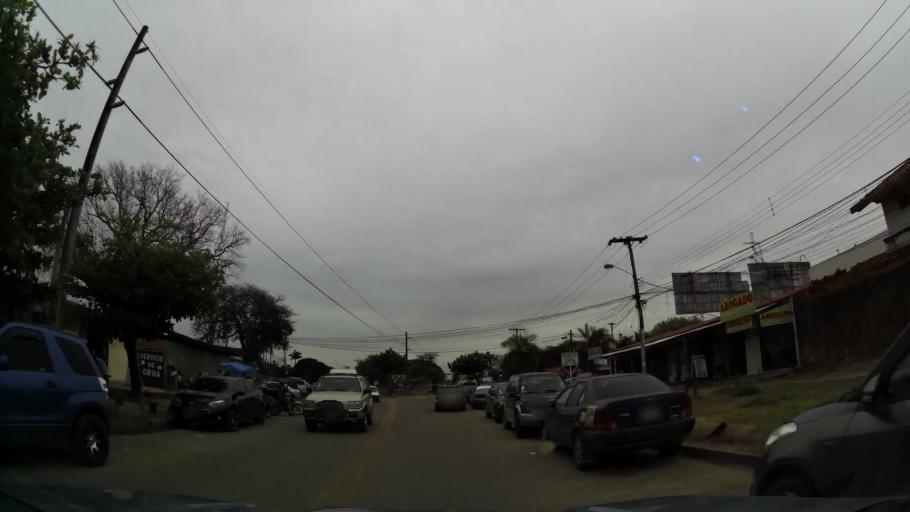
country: BO
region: Santa Cruz
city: Santa Cruz de la Sierra
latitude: -17.8122
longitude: -63.1815
